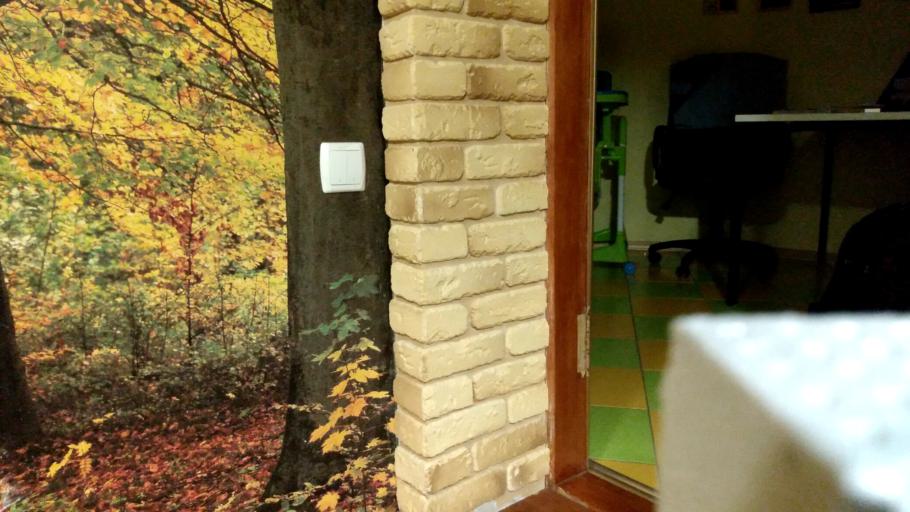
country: RU
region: Arkhangelskaya
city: Kargopol'
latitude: 61.4778
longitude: 37.7882
